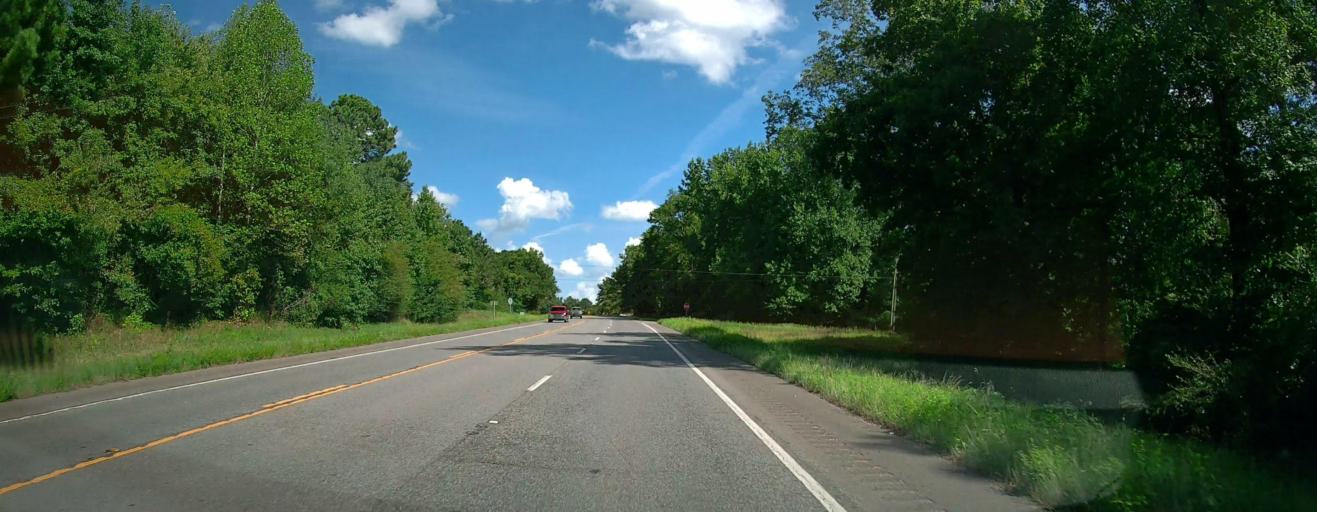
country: US
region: Alabama
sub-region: Pickens County
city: Gordo
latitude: 33.2927
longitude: -87.8729
